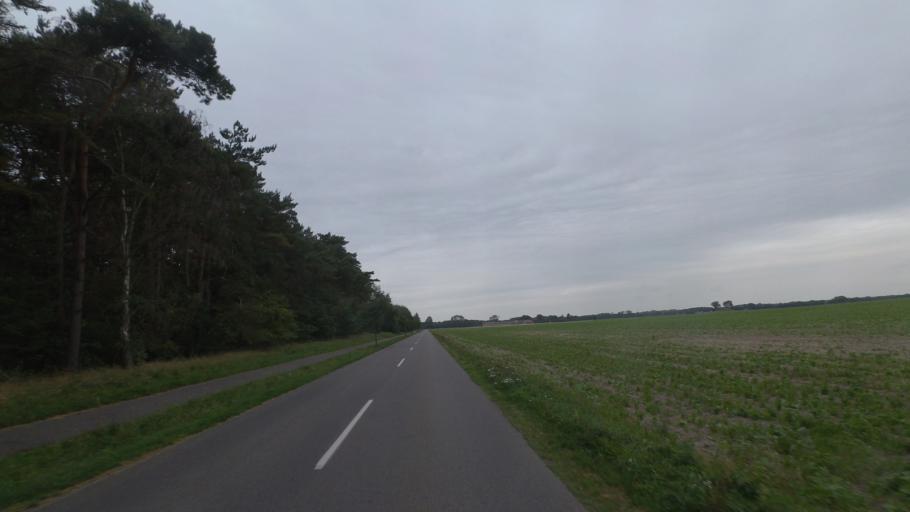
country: DK
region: Capital Region
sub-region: Bornholm Kommune
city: Akirkeby
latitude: 55.0026
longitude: 15.0171
